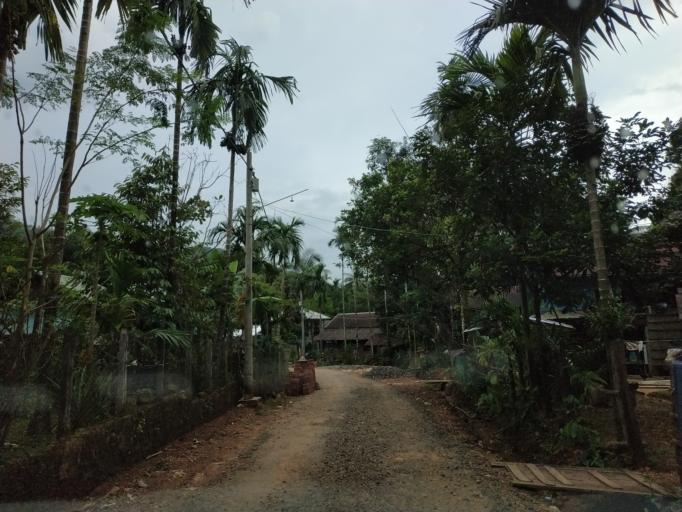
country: MM
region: Tanintharyi
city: Dawei
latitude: 13.8617
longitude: 98.2670
